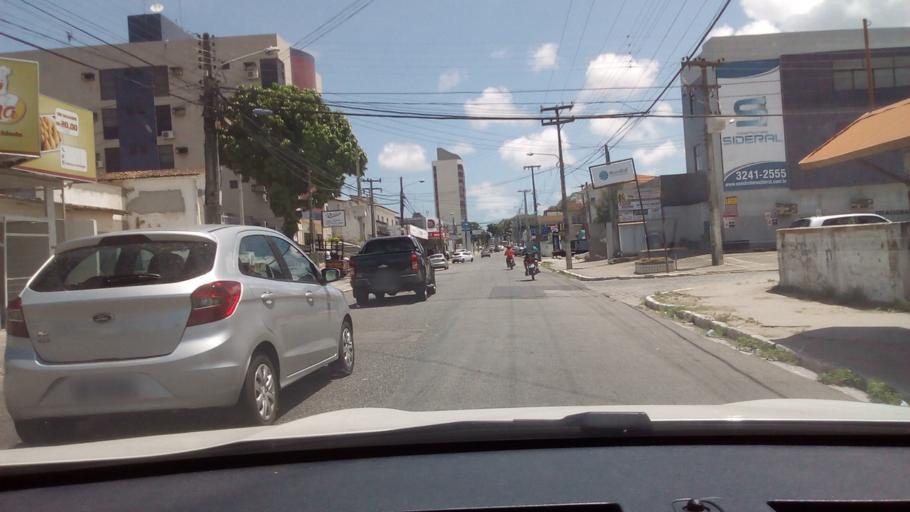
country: BR
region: Paraiba
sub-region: Joao Pessoa
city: Joao Pessoa
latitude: -7.1243
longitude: -34.8759
